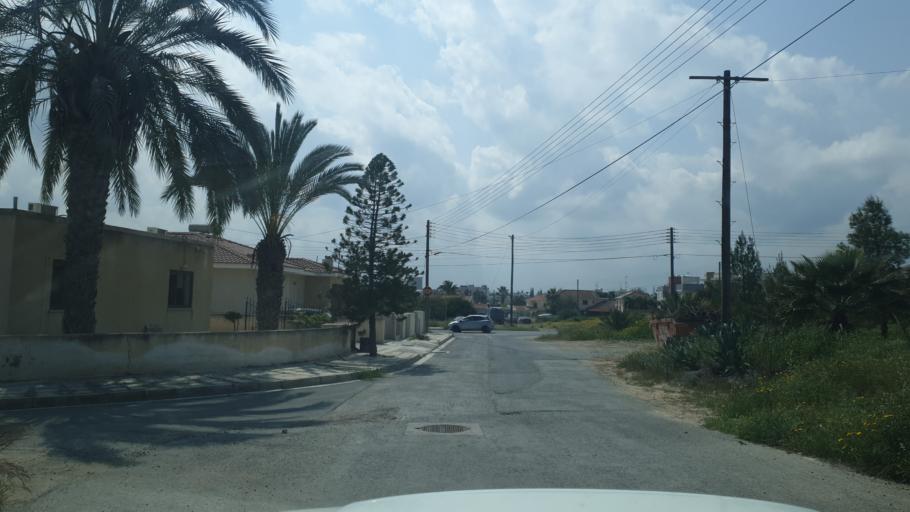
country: CY
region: Lefkosia
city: Geri
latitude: 35.1109
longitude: 33.4174
